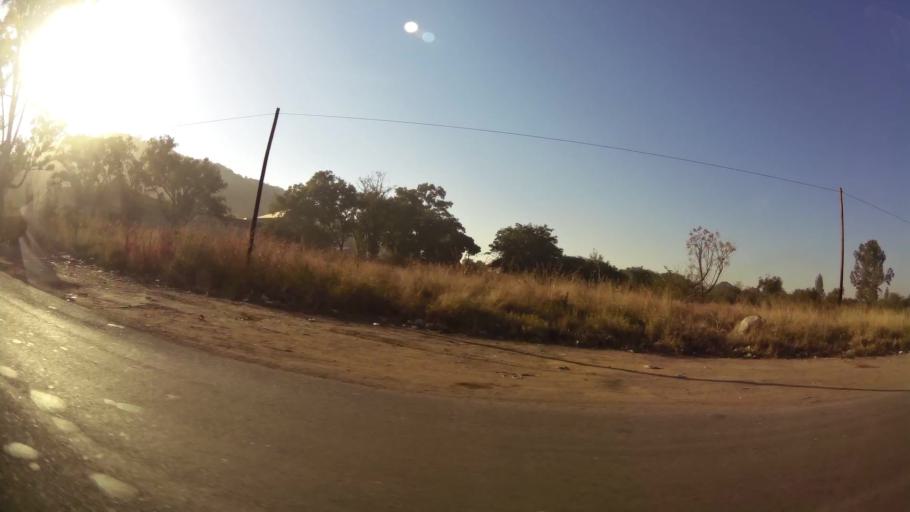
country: ZA
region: Gauteng
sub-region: City of Tshwane Metropolitan Municipality
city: Pretoria
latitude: -25.6305
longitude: 28.2052
